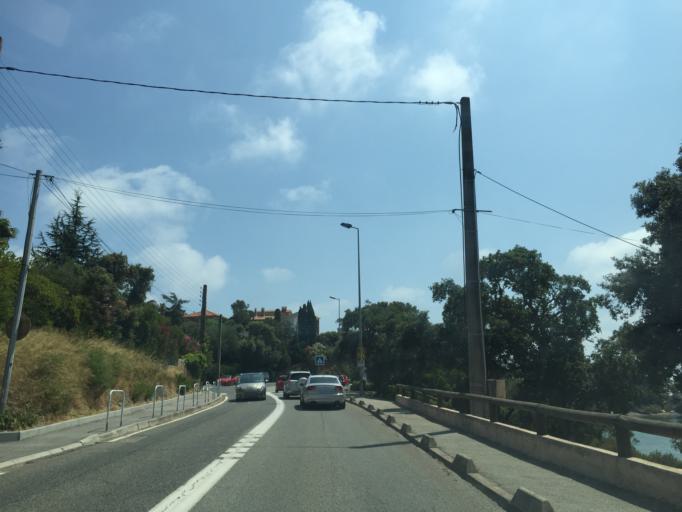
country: FR
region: Provence-Alpes-Cote d'Azur
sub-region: Departement du Var
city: Saint-Raphael
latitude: 43.4291
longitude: 6.8713
